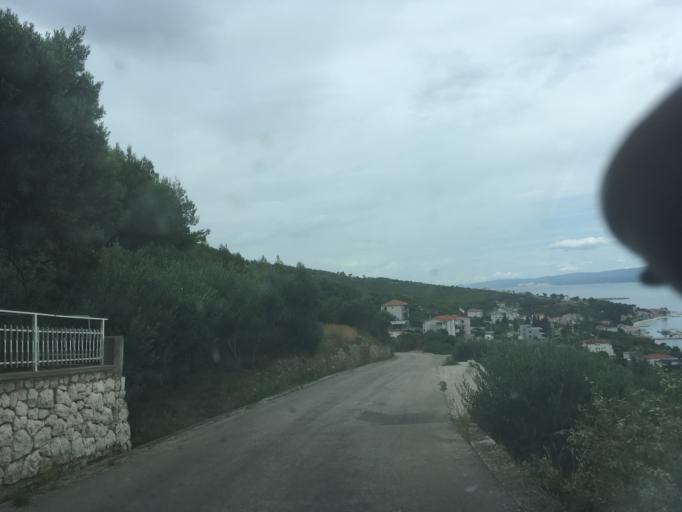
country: HR
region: Splitsko-Dalmatinska
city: Jesenice
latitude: 43.4583
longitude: 16.6185
